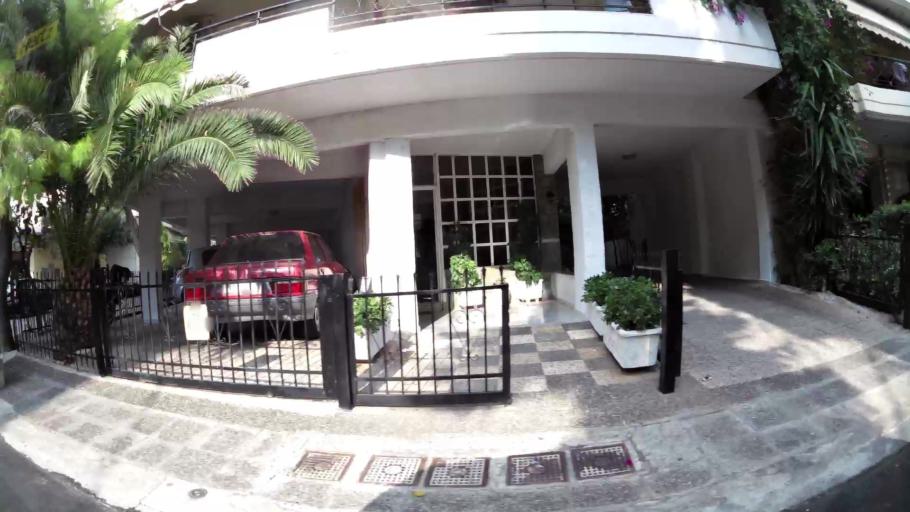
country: GR
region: Attica
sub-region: Nomarchia Athinas
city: Nea Smyrni
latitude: 37.9393
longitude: 23.7199
